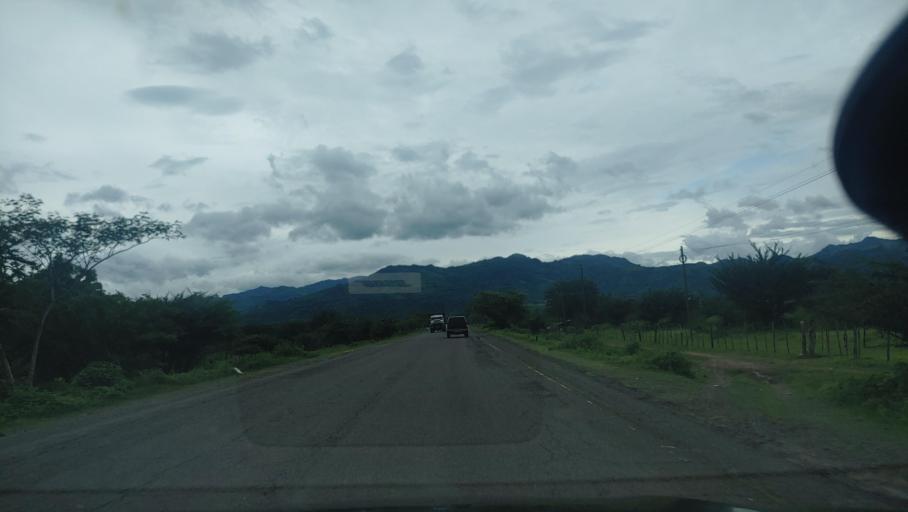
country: HN
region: Choluteca
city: Santa Ana de Yusguare
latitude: 13.3499
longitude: -87.1120
